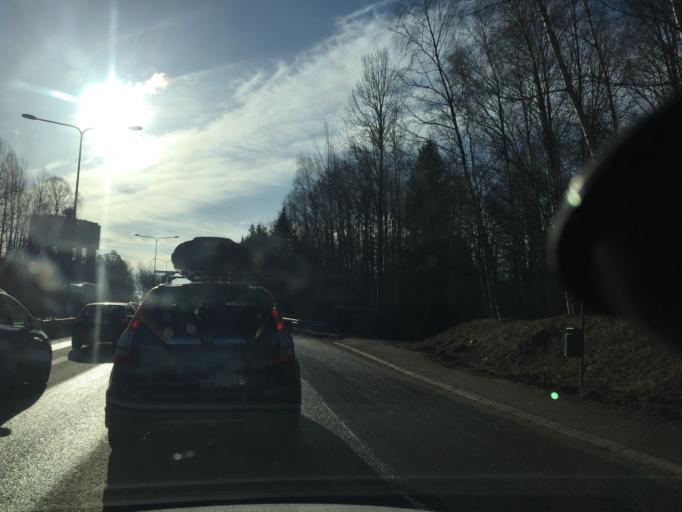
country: FI
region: Uusimaa
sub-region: Helsinki
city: Otaniemi
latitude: 60.1830
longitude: 24.8139
